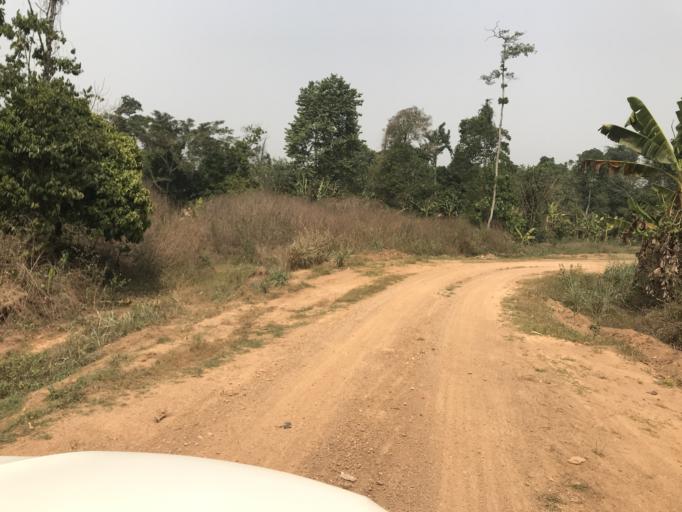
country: NG
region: Osun
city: Ifetedo
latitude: 7.0327
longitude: 4.4512
